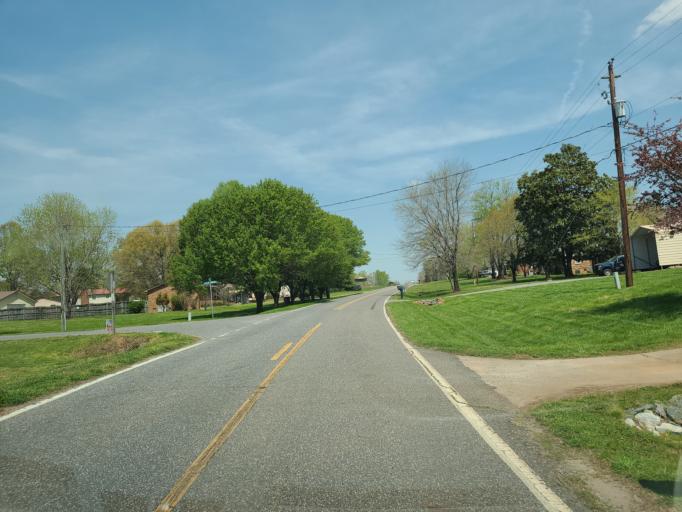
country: US
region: North Carolina
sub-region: Cleveland County
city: Shelby
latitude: 35.2547
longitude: -81.4847
